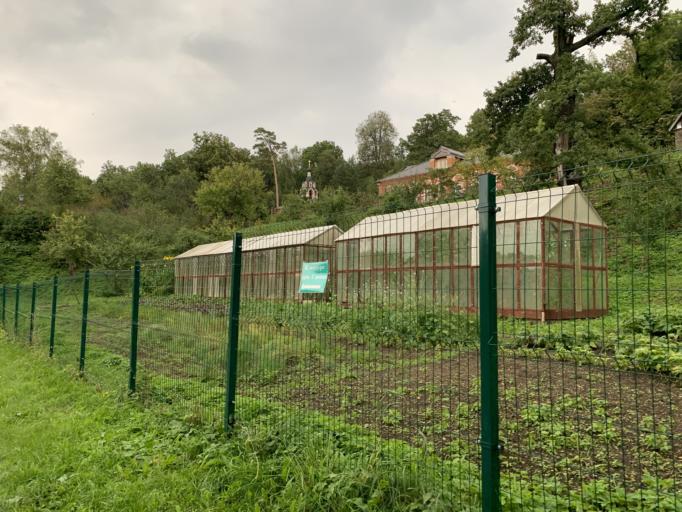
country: RU
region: Moskovskaya
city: Zvenigorod
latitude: 55.7359
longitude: 36.8120
